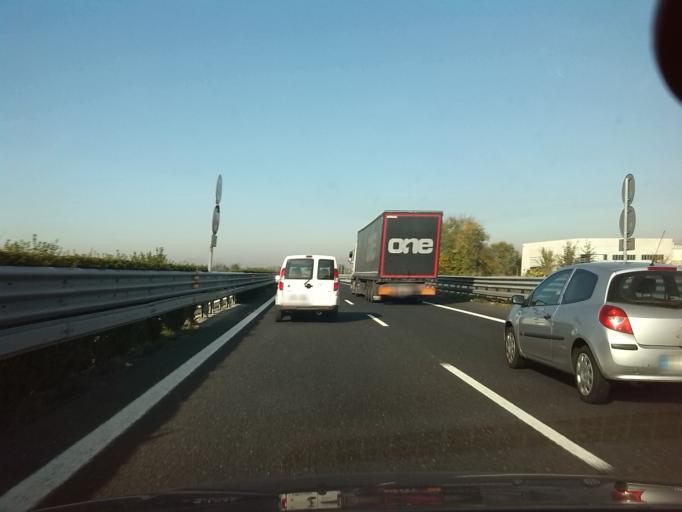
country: IT
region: Friuli Venezia Giulia
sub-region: Provincia di Udine
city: Lauzacco
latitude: 45.9751
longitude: 13.2461
